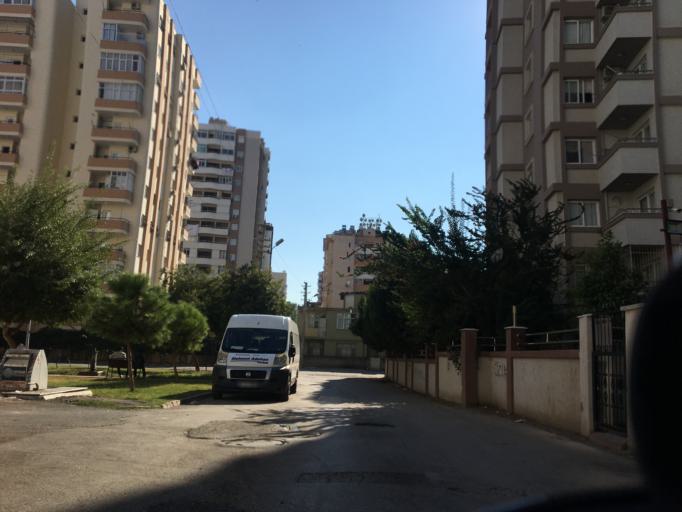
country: TR
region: Adana
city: Seyhan
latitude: 37.0261
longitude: 35.2855
